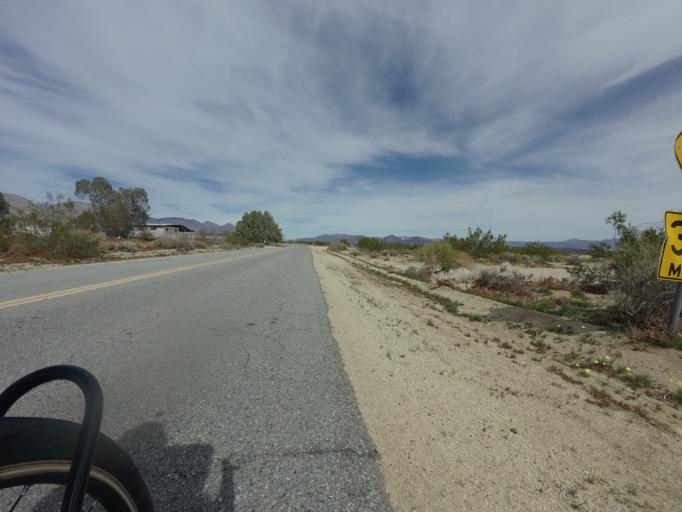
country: US
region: California
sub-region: Kern County
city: Inyokern
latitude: 35.7741
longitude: -117.8506
